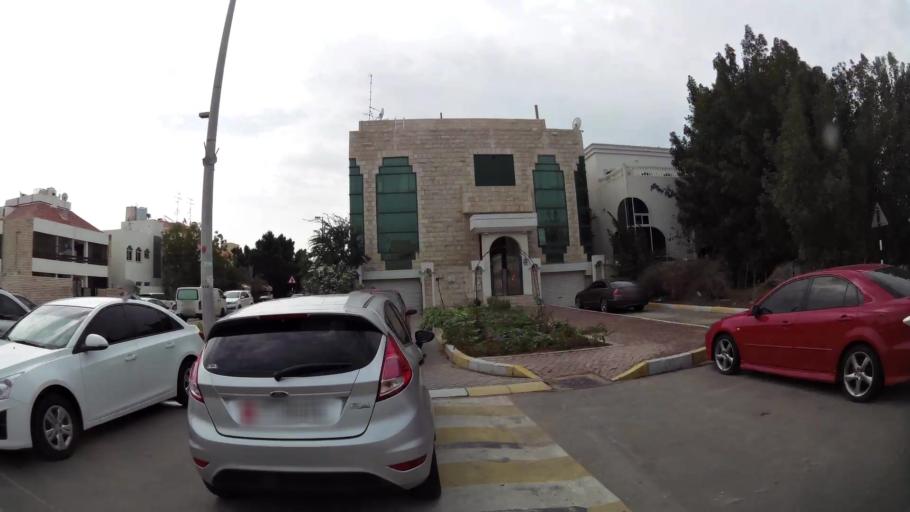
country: AE
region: Abu Dhabi
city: Abu Dhabi
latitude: 24.4397
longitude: 54.4384
